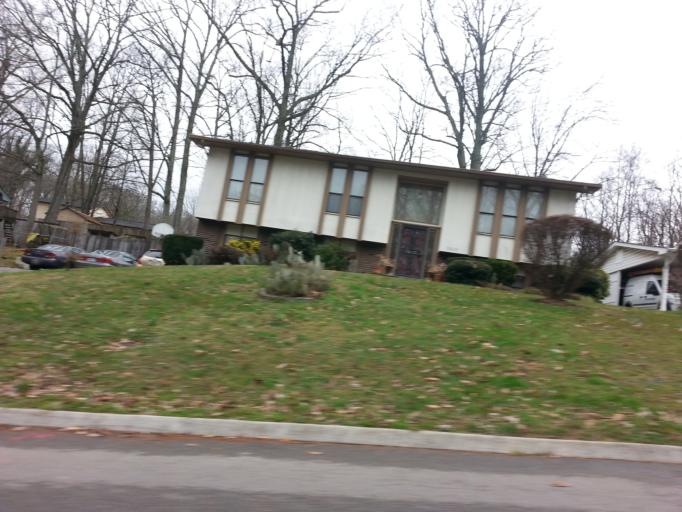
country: US
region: Tennessee
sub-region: Knox County
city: Knoxville
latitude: 35.9894
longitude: -84.0220
